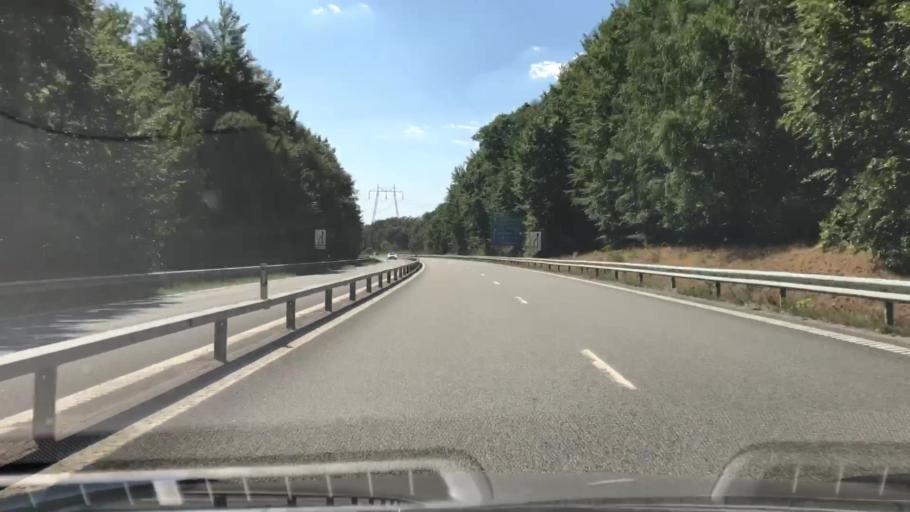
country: SE
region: Skane
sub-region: Horby Kommun
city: Hoerby
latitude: 55.8657
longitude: 13.6556
